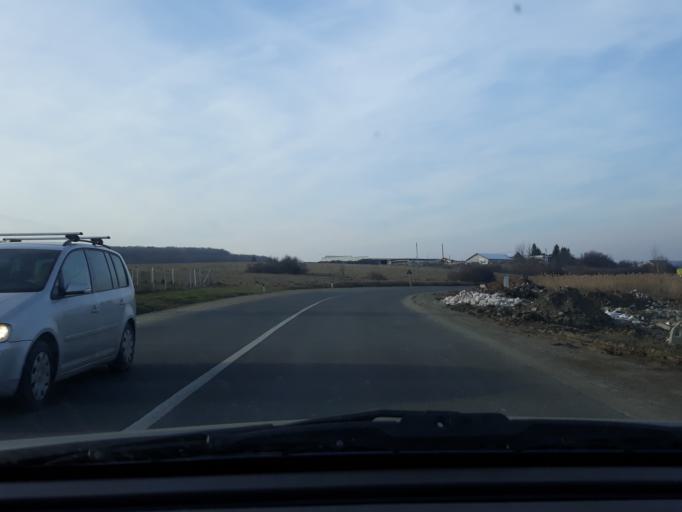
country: RO
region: Salaj
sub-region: Comuna Hereclean
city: Hereclean
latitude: 47.2296
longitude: 22.9994
